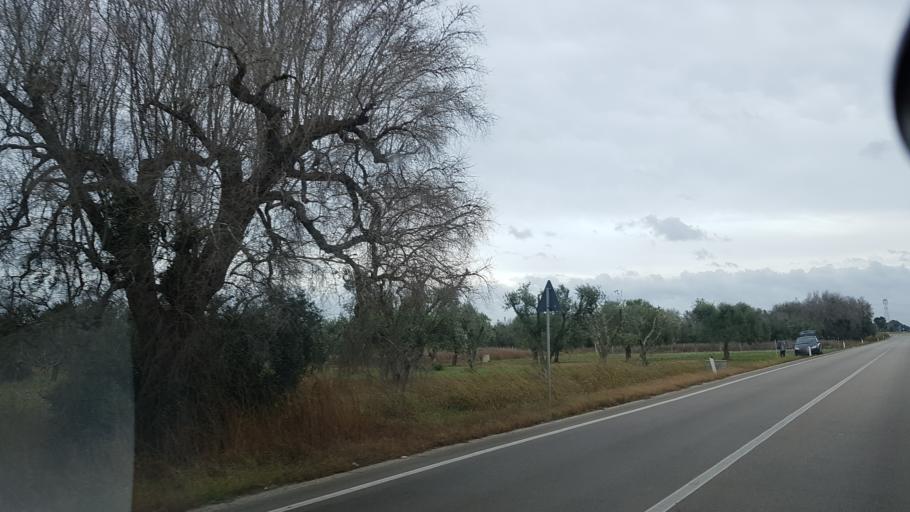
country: IT
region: Apulia
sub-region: Provincia di Lecce
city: Salice Salentino
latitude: 40.4007
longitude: 17.9673
